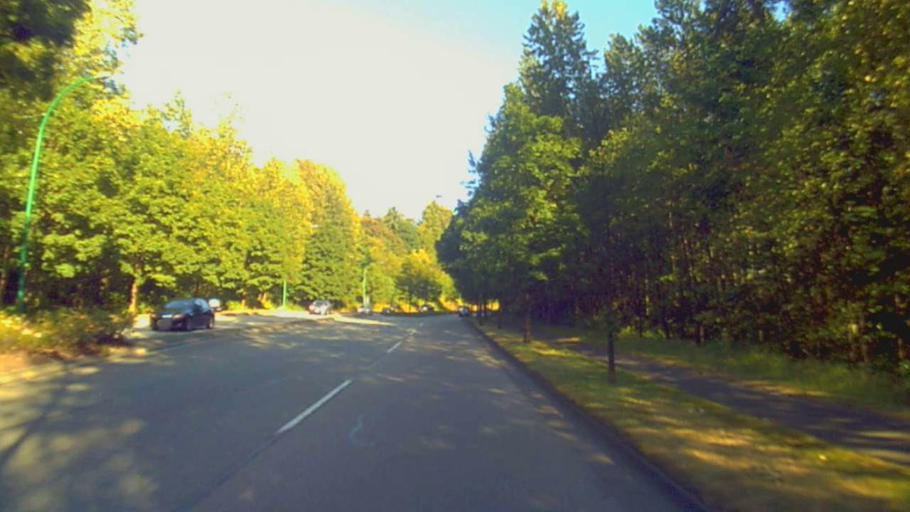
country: CA
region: British Columbia
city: New Westminster
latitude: 49.2419
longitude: -122.9079
